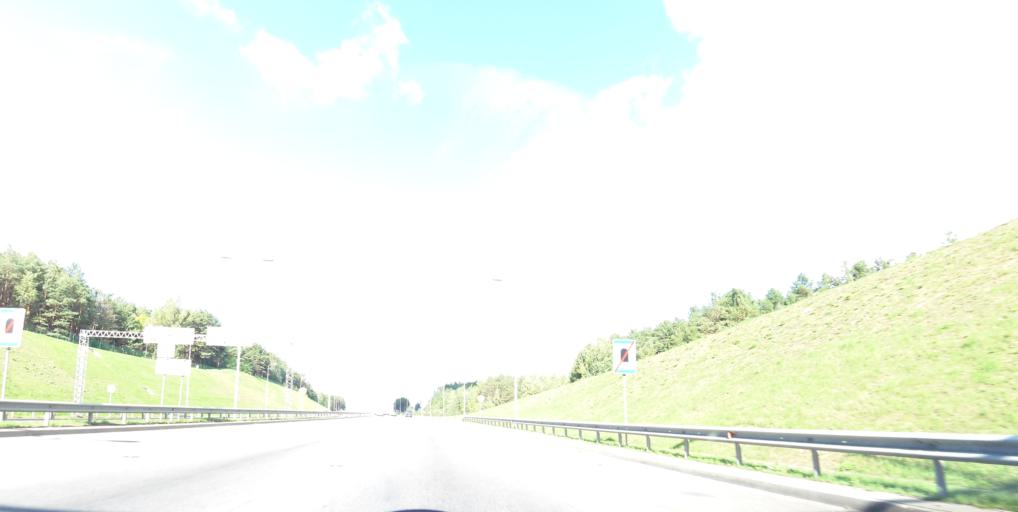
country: LT
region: Vilnius County
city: Lazdynai
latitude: 54.6751
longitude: 25.1963
